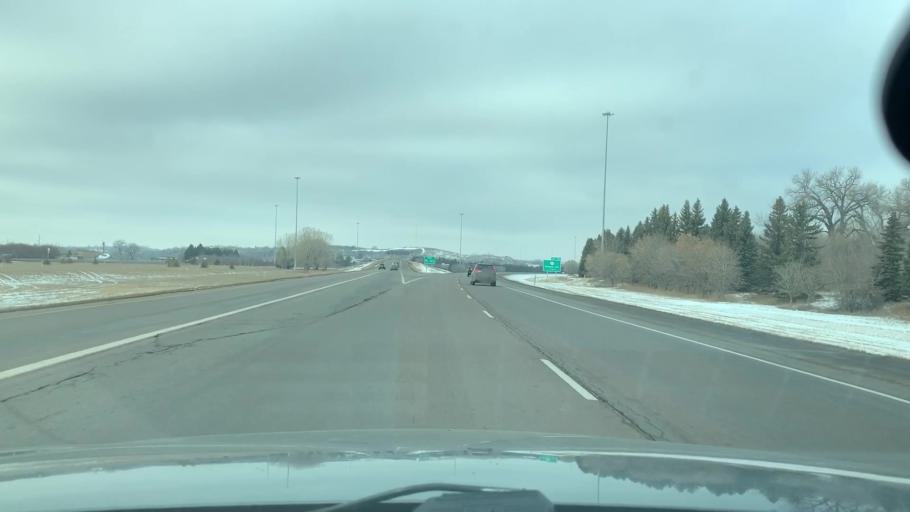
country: US
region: North Dakota
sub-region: Morton County
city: Mandan
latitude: 46.8259
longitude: -100.8517
